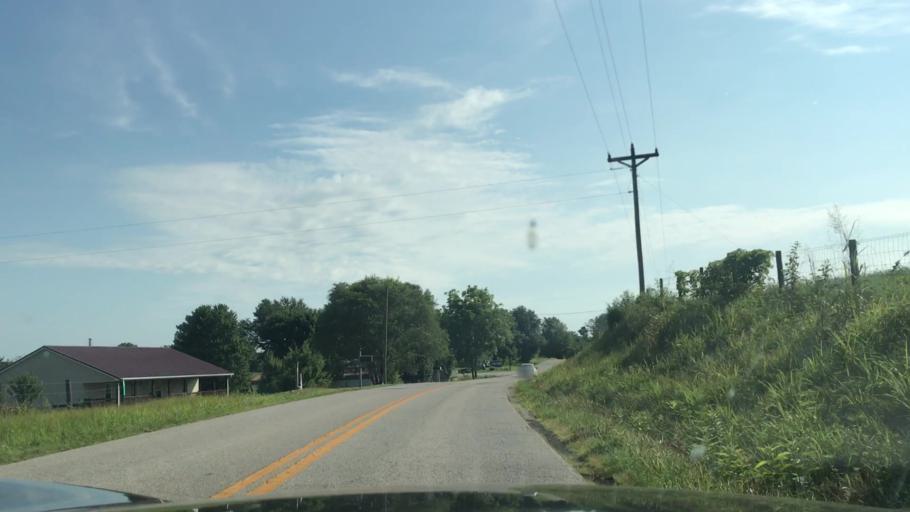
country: US
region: Kentucky
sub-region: Hart County
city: Munfordville
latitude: 37.2048
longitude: -85.7446
